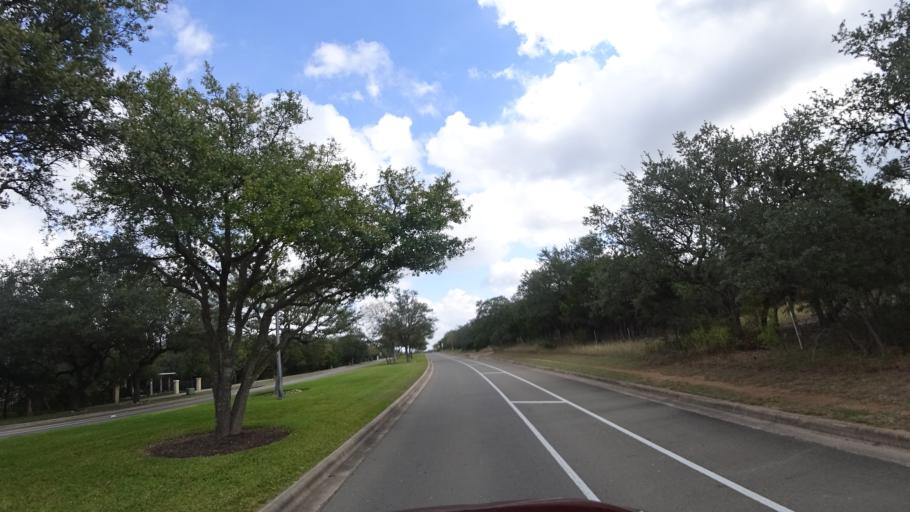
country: US
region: Texas
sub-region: Williamson County
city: Anderson Mill
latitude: 30.4180
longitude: -97.8585
